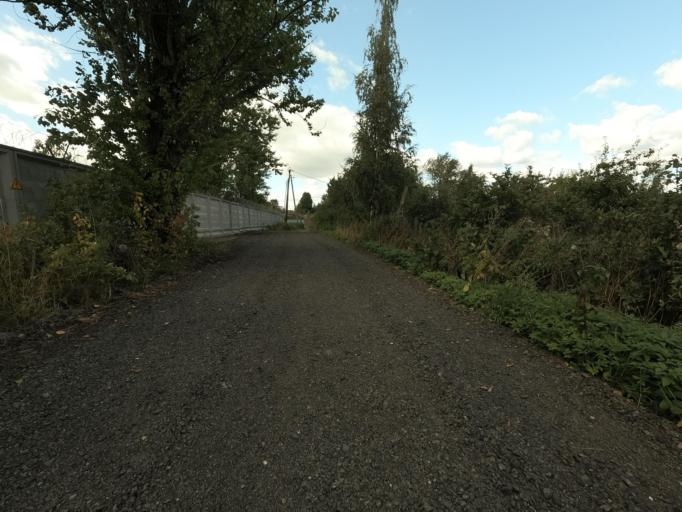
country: RU
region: St.-Petersburg
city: Krasnogvargeisky
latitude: 59.9686
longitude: 30.4962
